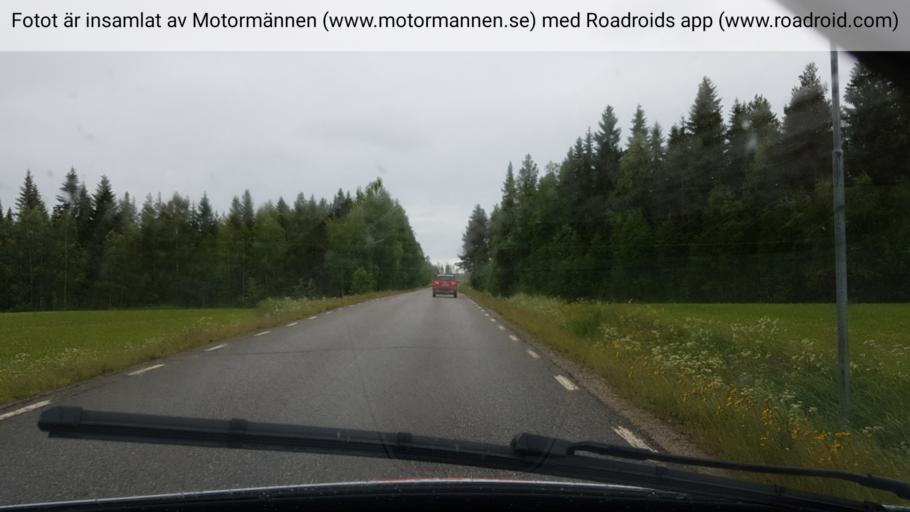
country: SE
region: Vaesterbotten
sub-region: Bjurholms Kommun
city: Bjurholm
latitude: 64.1451
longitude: 19.3147
